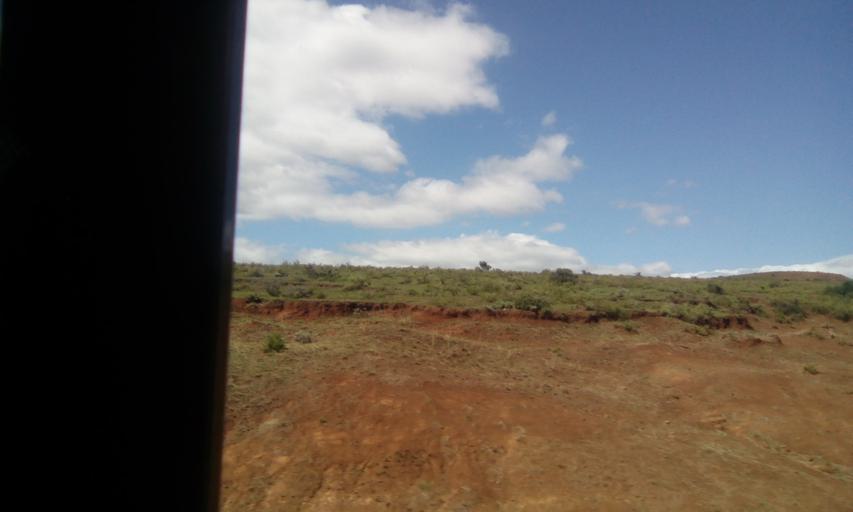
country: LS
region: Maseru
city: Nako
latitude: -29.6554
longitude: 27.8210
